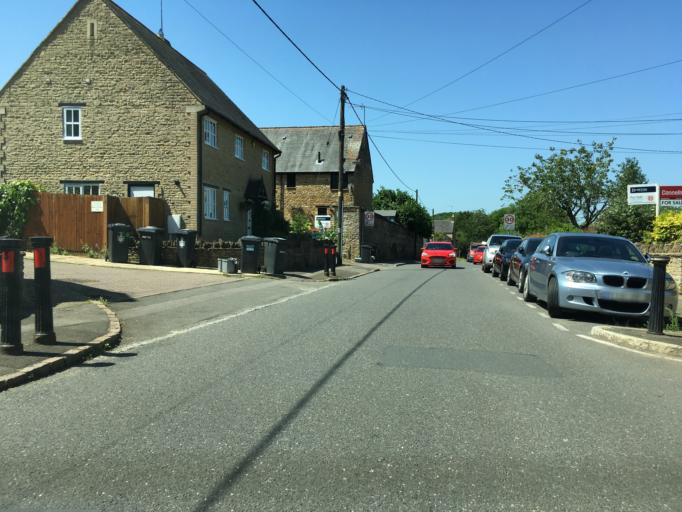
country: GB
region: England
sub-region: Northamptonshire
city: Brackley
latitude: 51.9975
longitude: -1.2117
